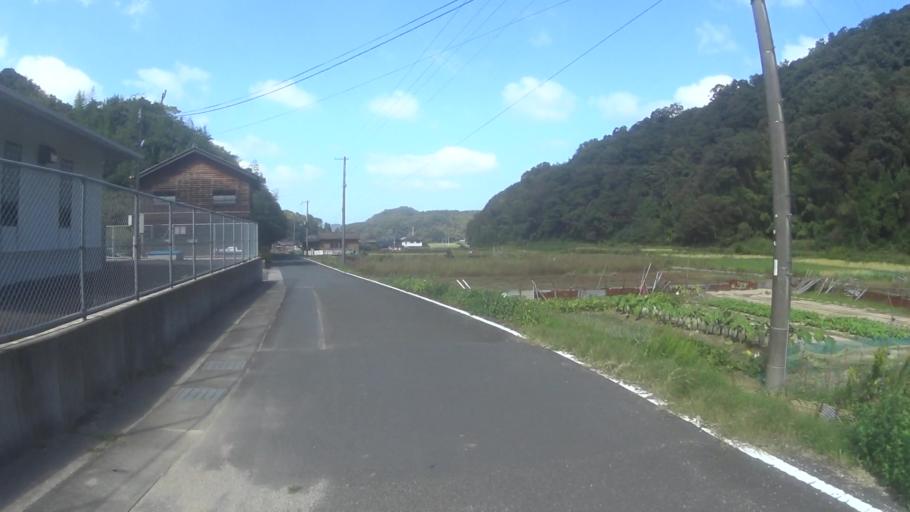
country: JP
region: Kyoto
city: Miyazu
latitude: 35.7076
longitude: 135.1186
